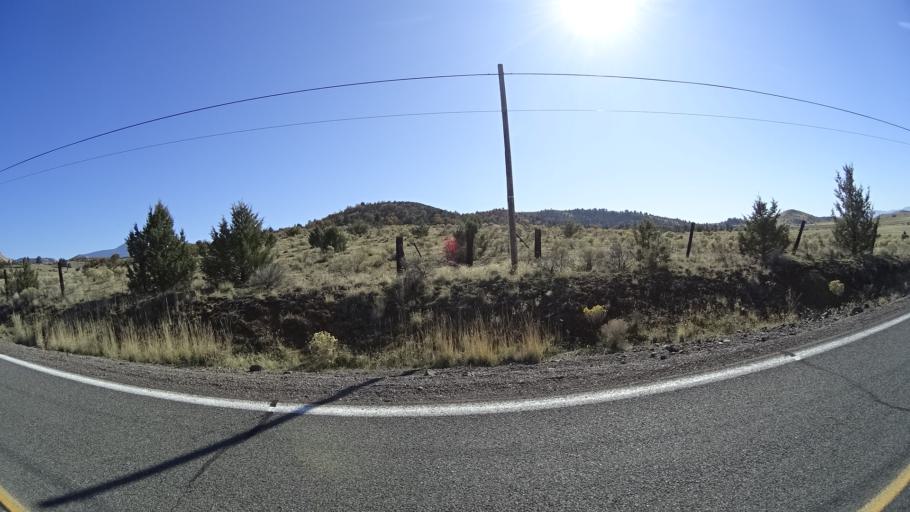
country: US
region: California
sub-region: Siskiyou County
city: Montague
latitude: 41.8046
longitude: -122.3954
